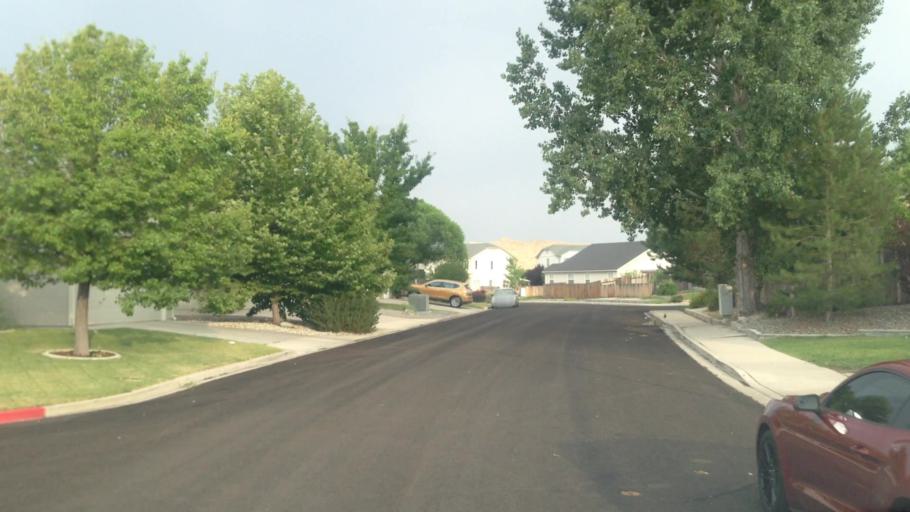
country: US
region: Nevada
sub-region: Washoe County
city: Lemmon Valley
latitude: 39.6337
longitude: -119.8722
